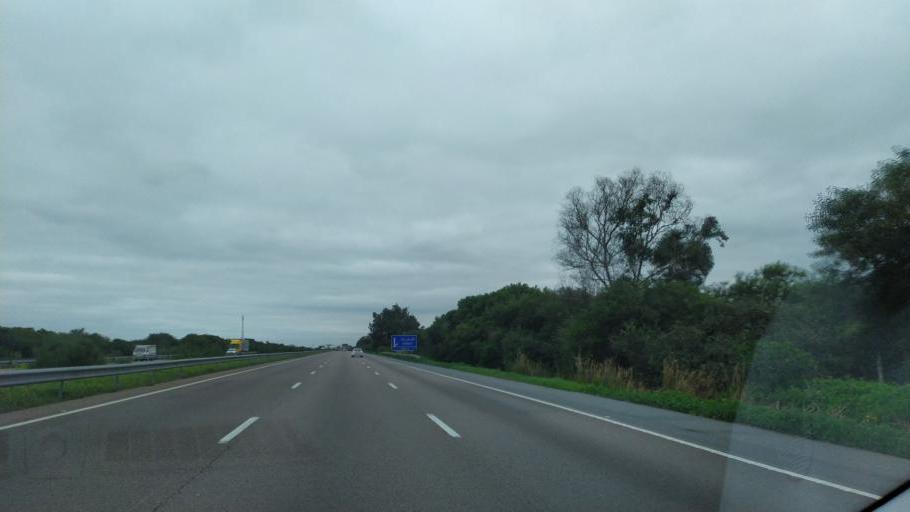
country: MA
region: Rabat-Sale-Zemmour-Zaer
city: Skhirat
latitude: 33.8313
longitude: -7.0988
